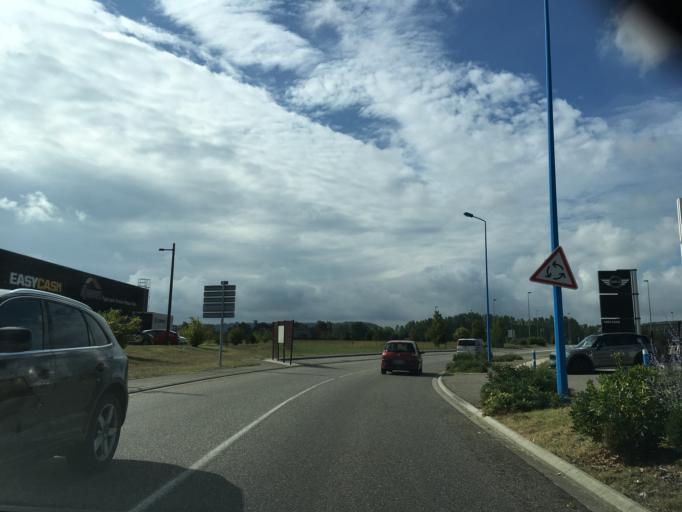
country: FR
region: Aquitaine
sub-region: Departement du Lot-et-Garonne
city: Boe
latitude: 44.1763
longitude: 0.6281
